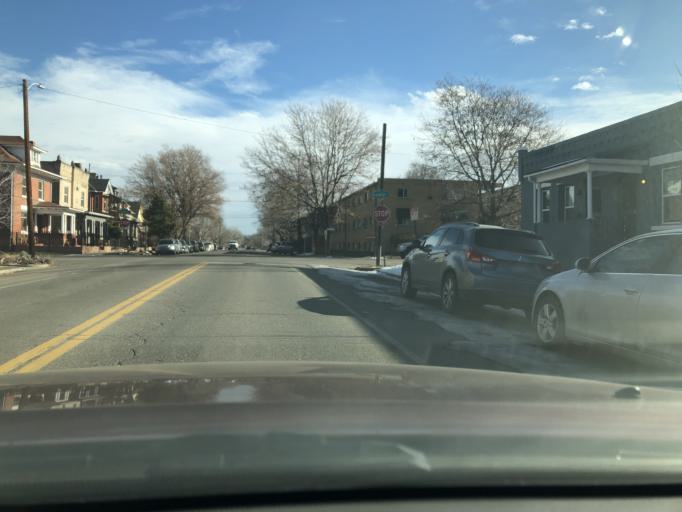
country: US
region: Colorado
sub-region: Denver County
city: Denver
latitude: 39.7494
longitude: -104.9689
